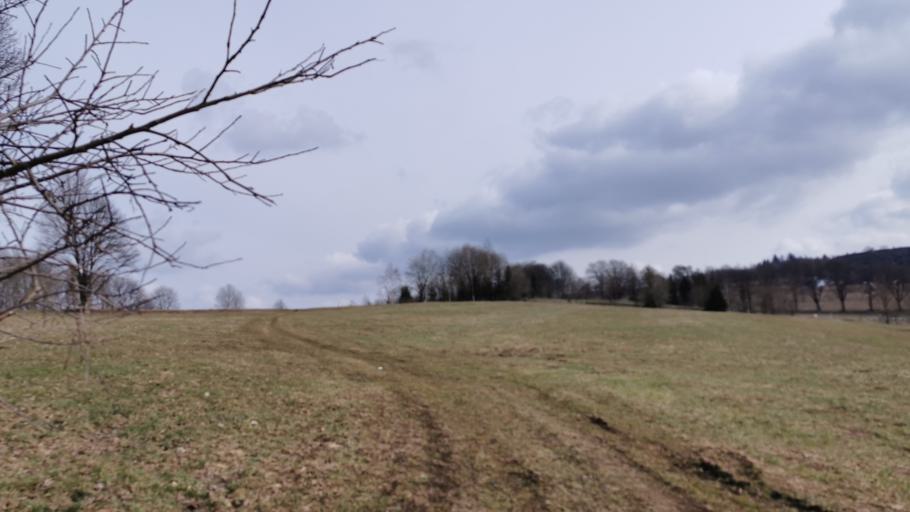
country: DE
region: Bavaria
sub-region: Upper Franconia
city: Ludwigsstadt
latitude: 50.4665
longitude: 11.4269
